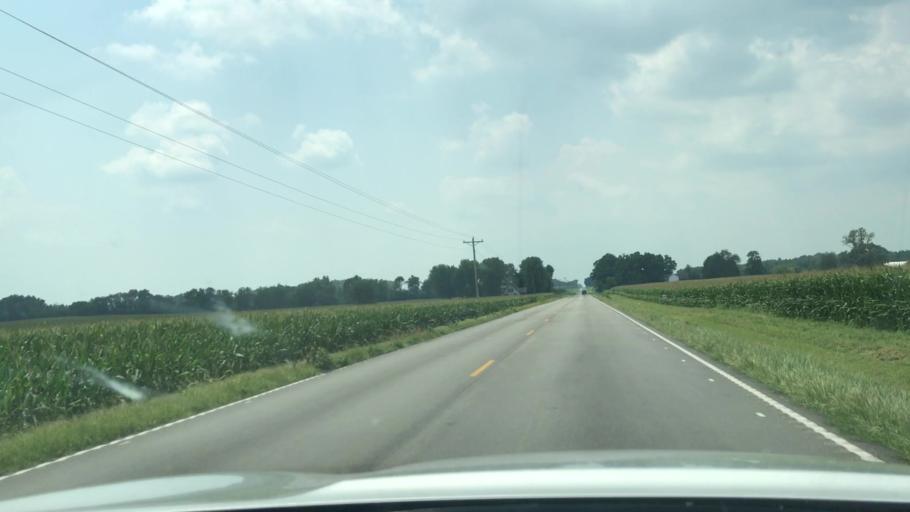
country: US
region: Kentucky
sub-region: Todd County
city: Guthrie
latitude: 36.6983
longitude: -87.1196
